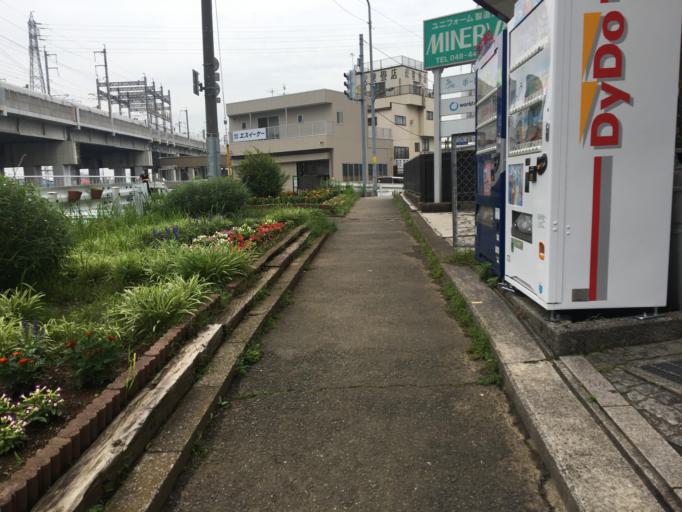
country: JP
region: Saitama
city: Shimotoda
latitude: 35.8047
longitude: 139.6811
